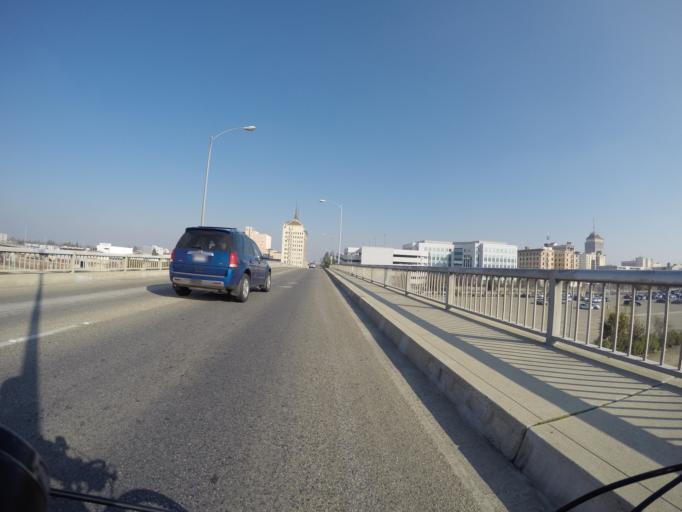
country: US
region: California
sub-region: Fresno County
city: Fresno
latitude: 36.7357
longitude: -119.7974
